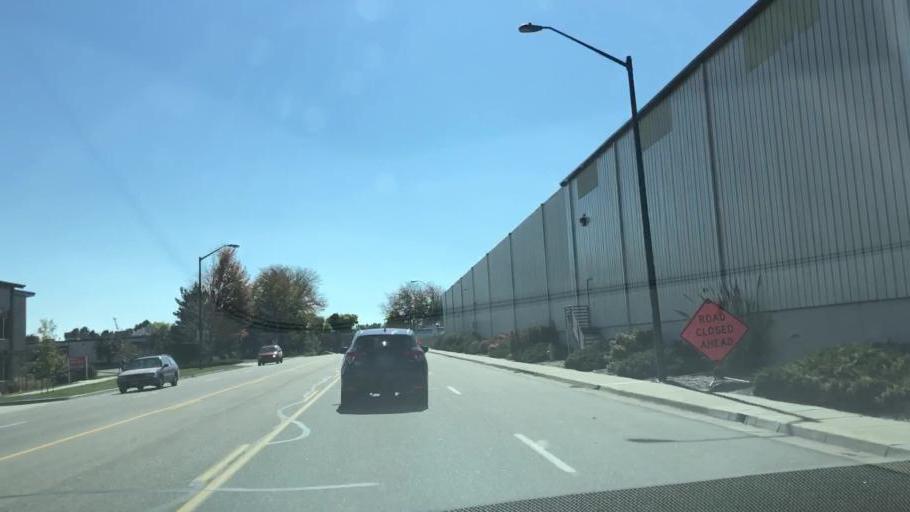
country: US
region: Colorado
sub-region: Larimer County
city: Fort Collins
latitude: 40.5695
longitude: -105.0452
